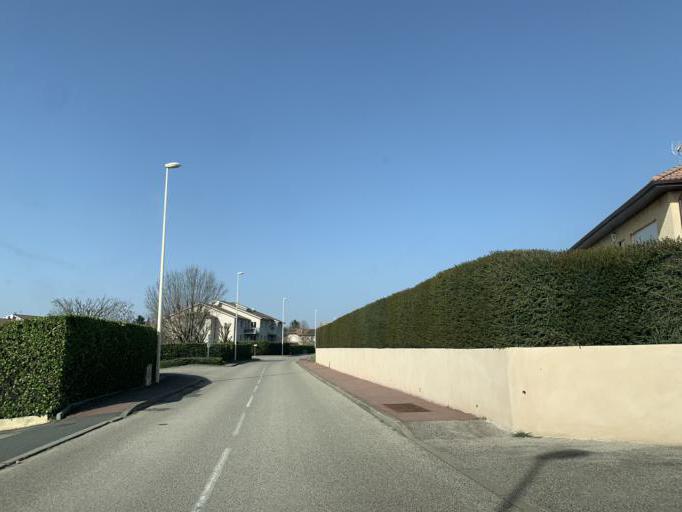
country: FR
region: Rhone-Alpes
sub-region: Departement du Rhone
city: Rillieux-la-Pape
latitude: 45.8218
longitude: 4.9270
